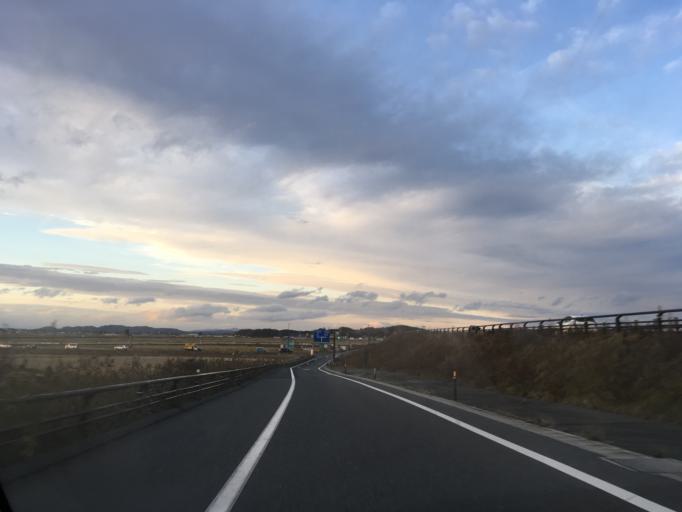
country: JP
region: Miyagi
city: Wakuya
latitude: 38.6748
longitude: 141.2654
